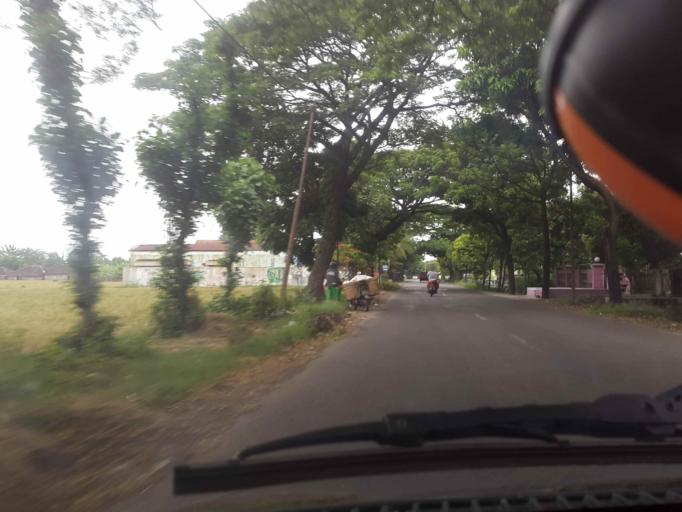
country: ID
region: Central Java
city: Sragen
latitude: -7.4369
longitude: 111.0167
